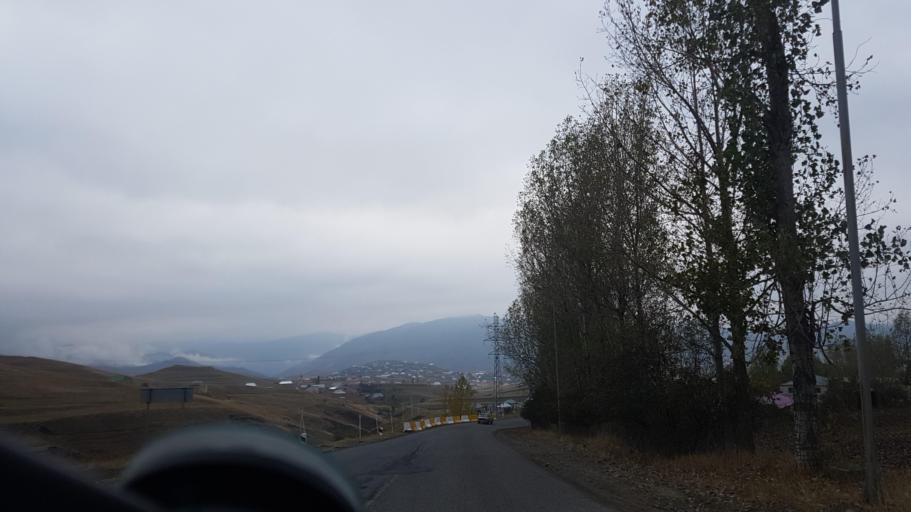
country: AZ
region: Gadabay Rayon
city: Ariqdam
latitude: 40.6133
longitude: 45.8121
